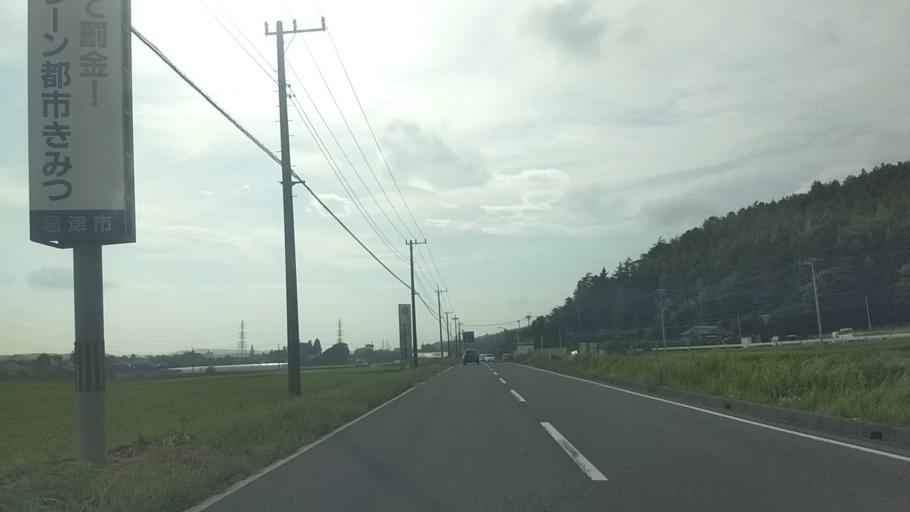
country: JP
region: Chiba
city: Kisarazu
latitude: 35.3097
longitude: 139.9722
